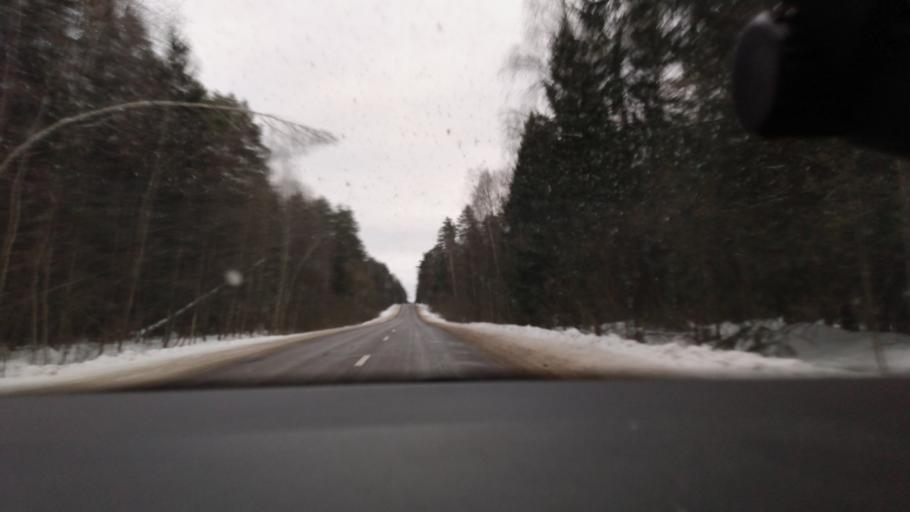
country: RU
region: Moskovskaya
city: Yegor'yevsk
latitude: 55.2204
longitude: 39.0778
